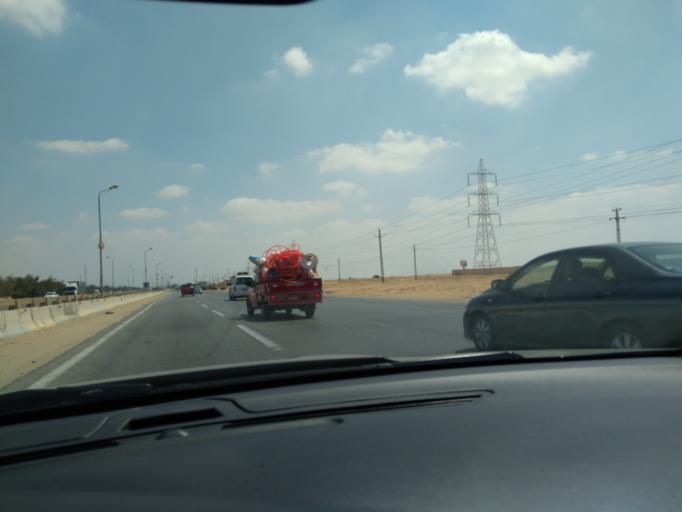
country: EG
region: Al Isma'iliyah
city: At Tall al Kabir
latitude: 30.4015
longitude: 31.9880
